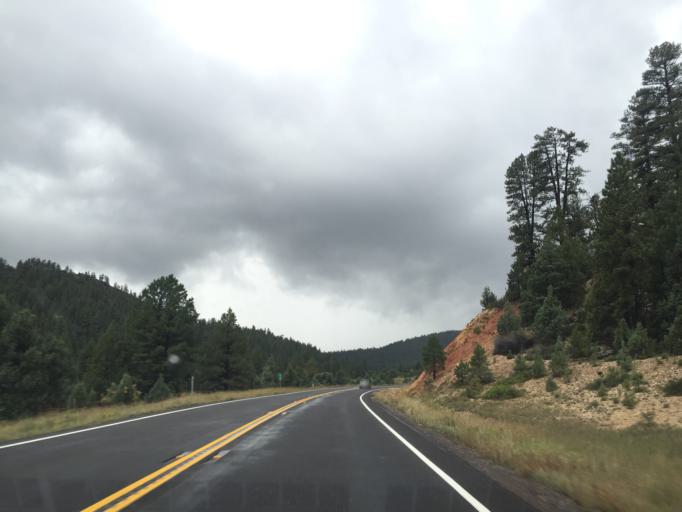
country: US
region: Utah
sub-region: Garfield County
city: Panguitch
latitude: 37.4543
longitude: -112.5273
